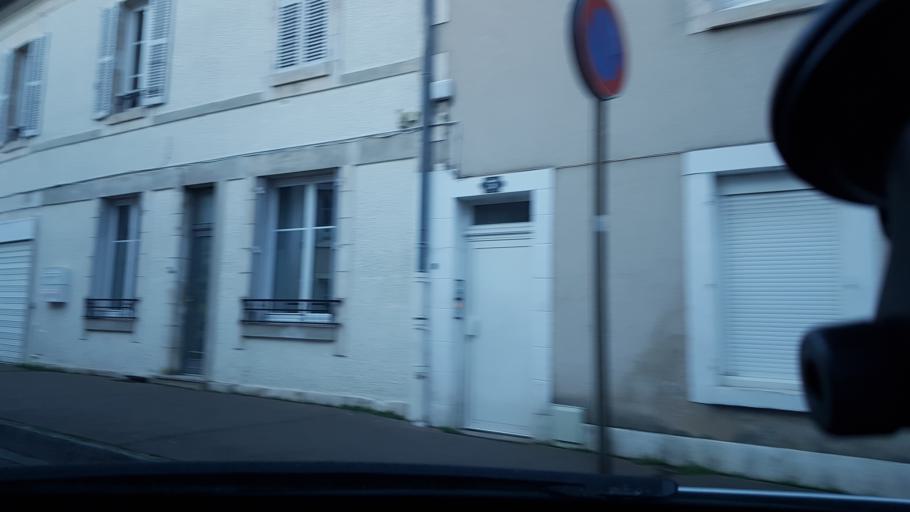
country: FR
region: Centre
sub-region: Departement du Cher
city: Bourges
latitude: 47.0792
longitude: 2.4025
